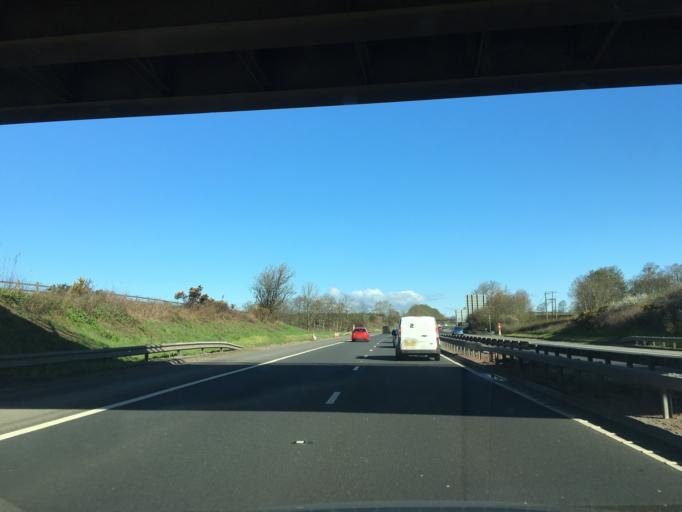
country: GB
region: Scotland
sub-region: Stirling
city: Stirling
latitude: 56.0884
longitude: -3.9454
